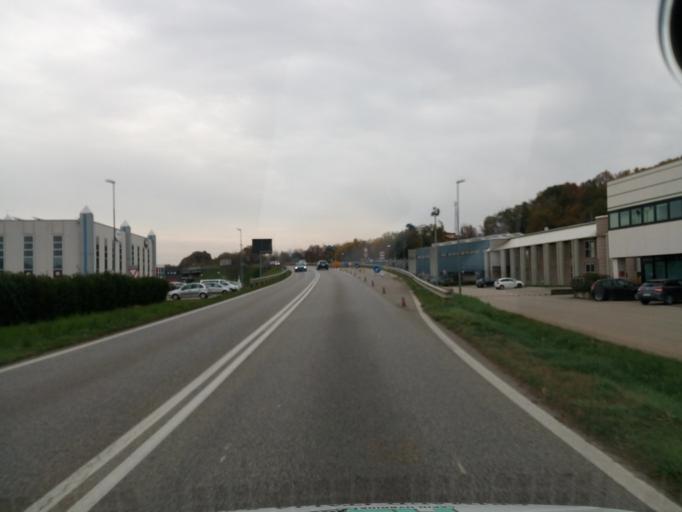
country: IT
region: Veneto
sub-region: Provincia di Treviso
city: Montebelluna
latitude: 45.7854
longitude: 12.0493
